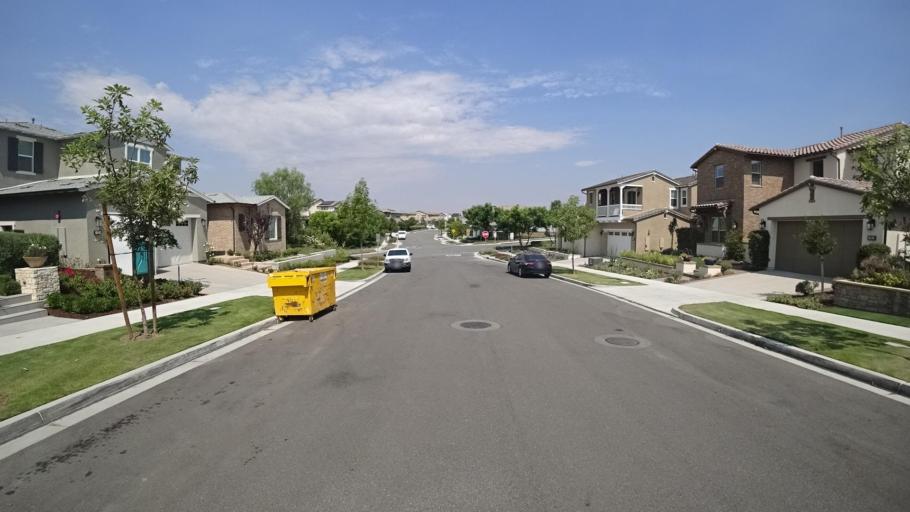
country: US
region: California
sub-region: Orange County
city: Ladera Ranch
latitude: 33.5382
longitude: -117.6045
